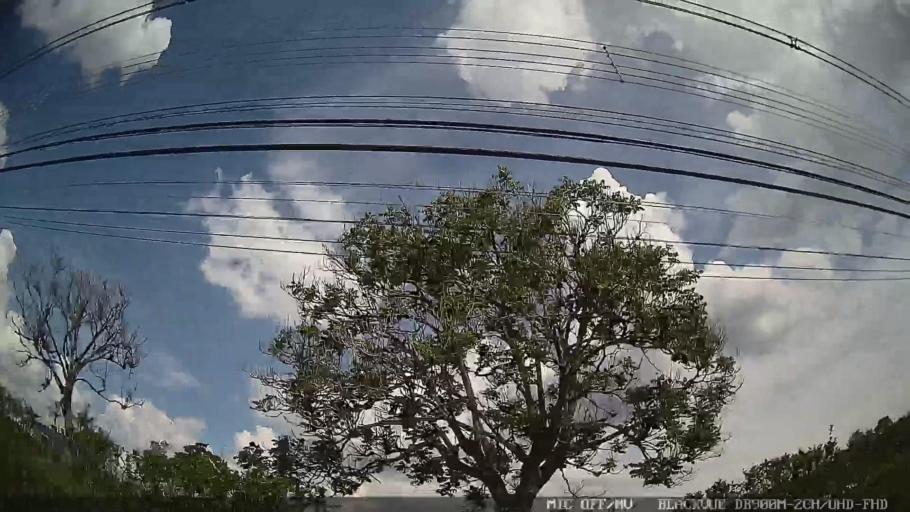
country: BR
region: Sao Paulo
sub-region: Braganca Paulista
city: Braganca Paulista
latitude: -22.9759
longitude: -46.5537
